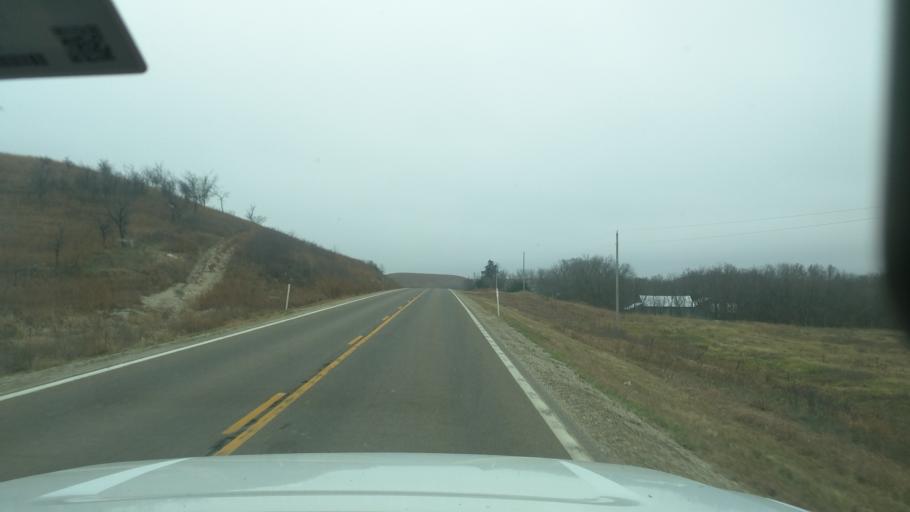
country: US
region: Kansas
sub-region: Riley County
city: Manhattan
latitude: 39.0017
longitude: -96.5243
